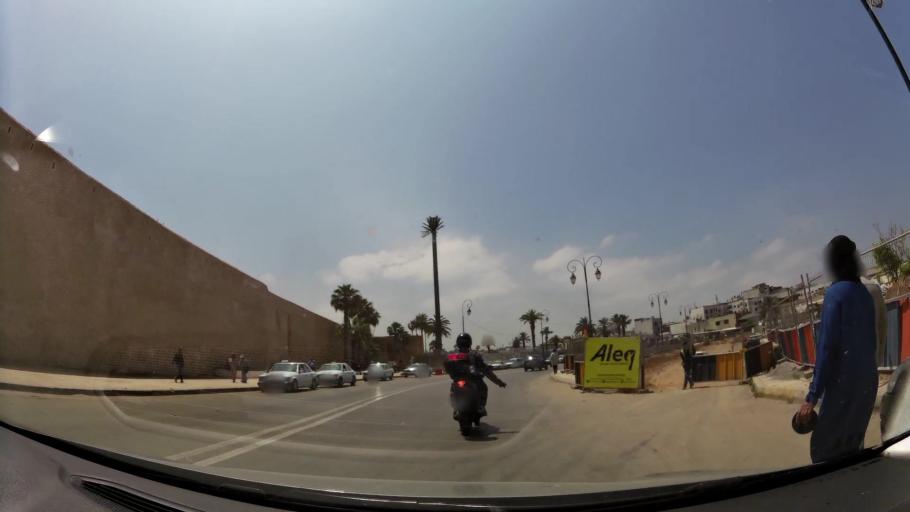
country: MA
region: Rabat-Sale-Zemmour-Zaer
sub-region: Rabat
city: Rabat
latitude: 34.0233
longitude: -6.8410
